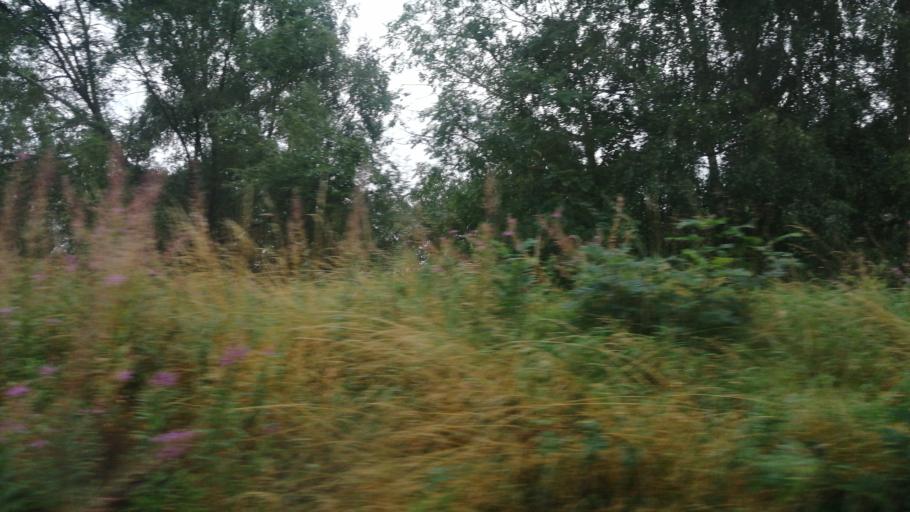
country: GB
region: Scotland
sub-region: Highland
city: Evanton
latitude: 57.6294
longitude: -4.3712
